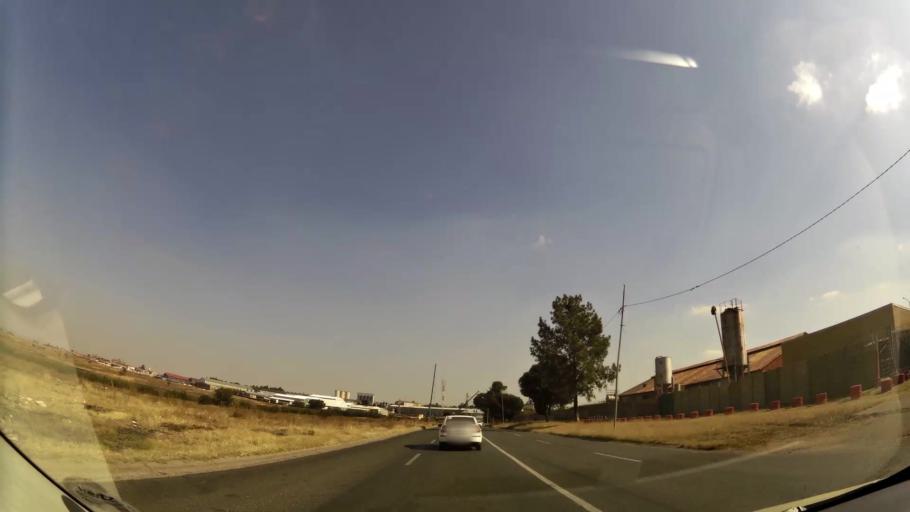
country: ZA
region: Gauteng
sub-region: City of Johannesburg Metropolitan Municipality
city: Roodepoort
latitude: -26.1555
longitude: 27.8073
